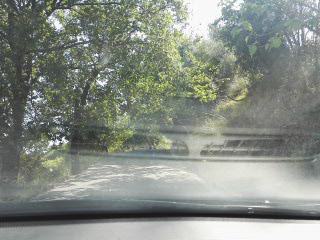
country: IT
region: Calabria
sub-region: Provincia di Reggio Calabria
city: Stilo
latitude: 38.4535
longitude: 16.4621
